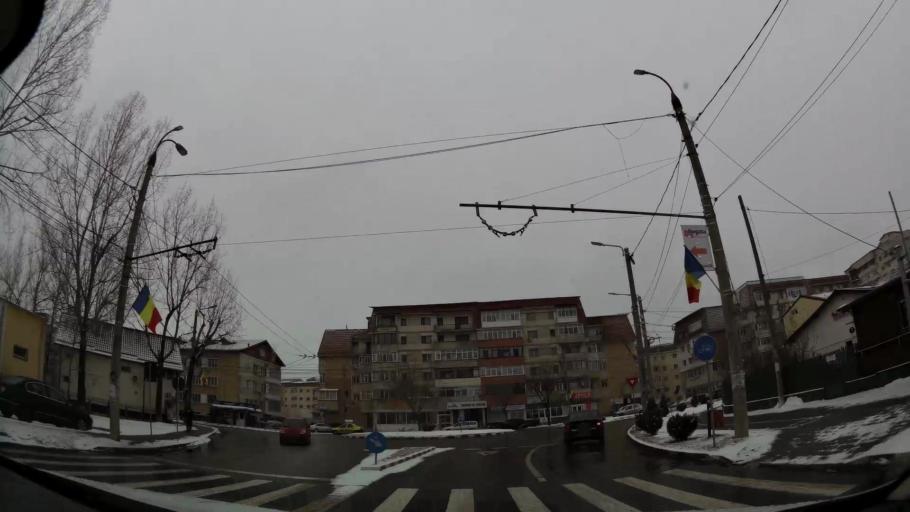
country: RO
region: Dambovita
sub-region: Municipiul Targoviste
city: Targoviste
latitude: 44.9180
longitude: 25.4678
